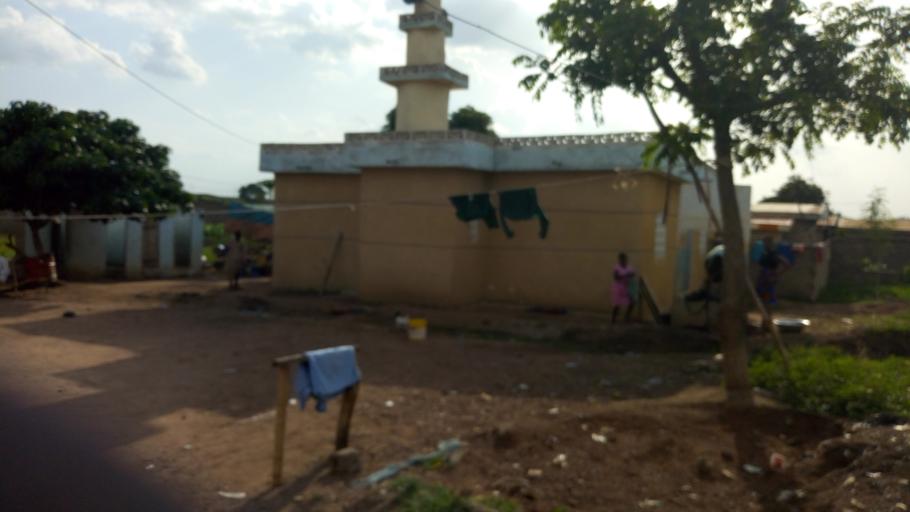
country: CI
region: Vallee du Bandama
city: Bouake
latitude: 7.7274
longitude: -5.0002
